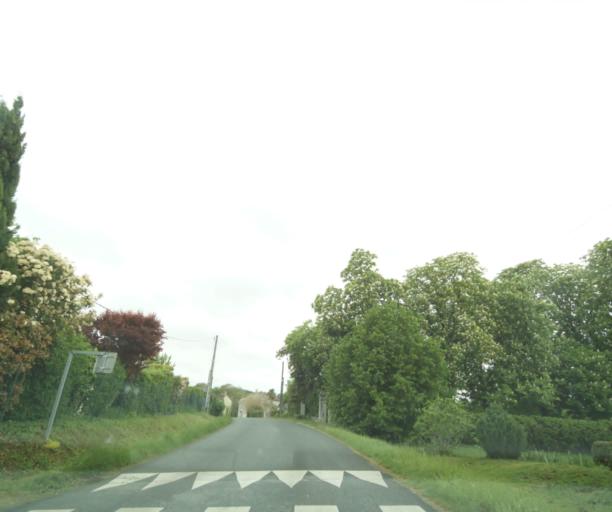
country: FR
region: Poitou-Charentes
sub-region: Departement de la Charente-Maritime
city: Chaniers
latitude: 45.7003
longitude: -0.5464
